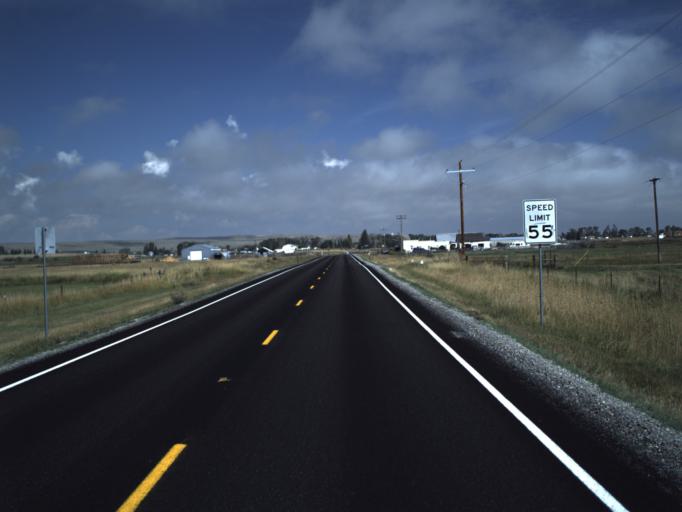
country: US
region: Utah
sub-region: Rich County
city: Randolph
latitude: 41.6501
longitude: -111.1843
